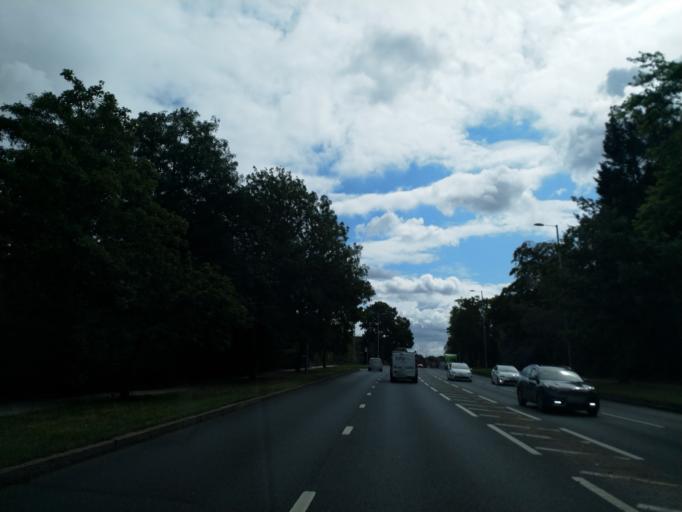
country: GB
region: England
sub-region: Greater London
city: Belsize Park
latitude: 51.5848
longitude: -0.1723
